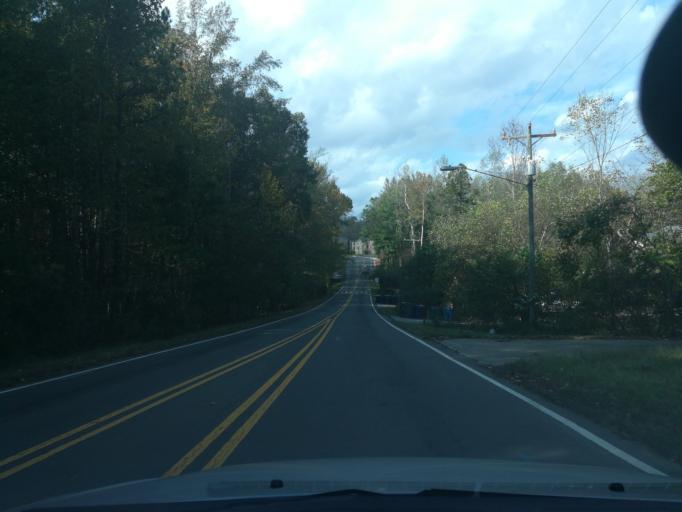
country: US
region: North Carolina
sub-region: Durham County
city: Durham
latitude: 36.0549
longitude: -78.9351
